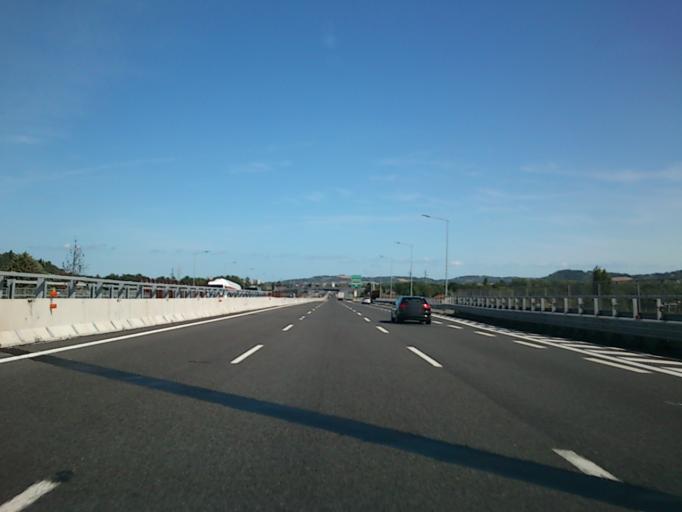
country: IT
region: The Marches
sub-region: Provincia di Pesaro e Urbino
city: Villa Ceccolini
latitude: 43.8990
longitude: 12.8396
